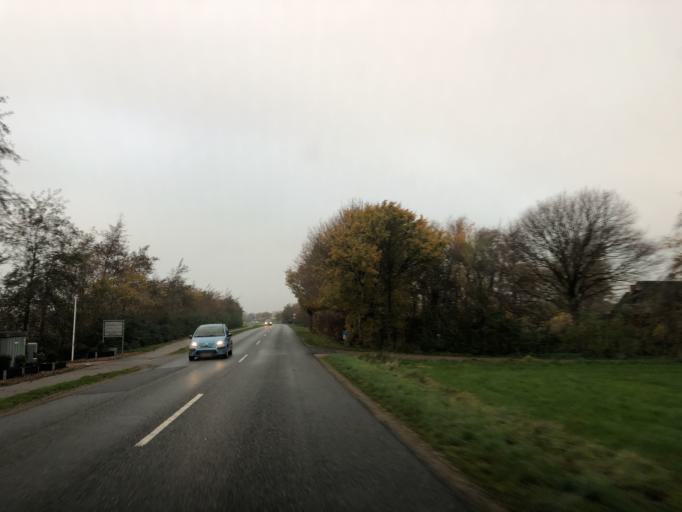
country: DK
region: Central Jutland
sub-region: Herning Kommune
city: Vildbjerg
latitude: 56.2192
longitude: 8.7394
